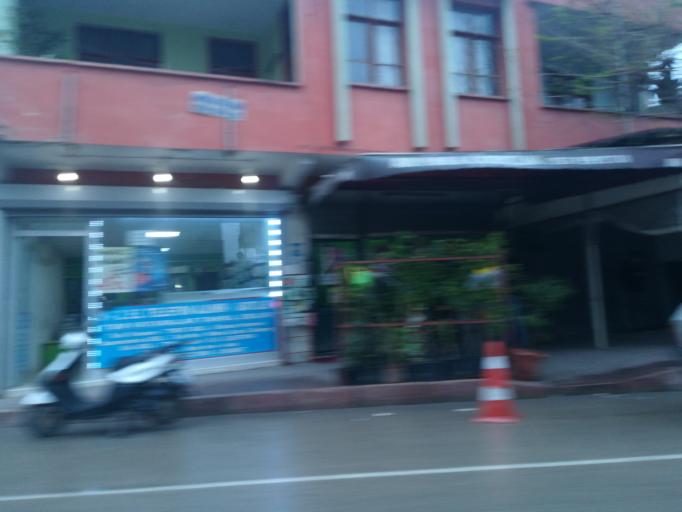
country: TR
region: Adana
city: Seyhan
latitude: 37.0148
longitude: 35.2765
